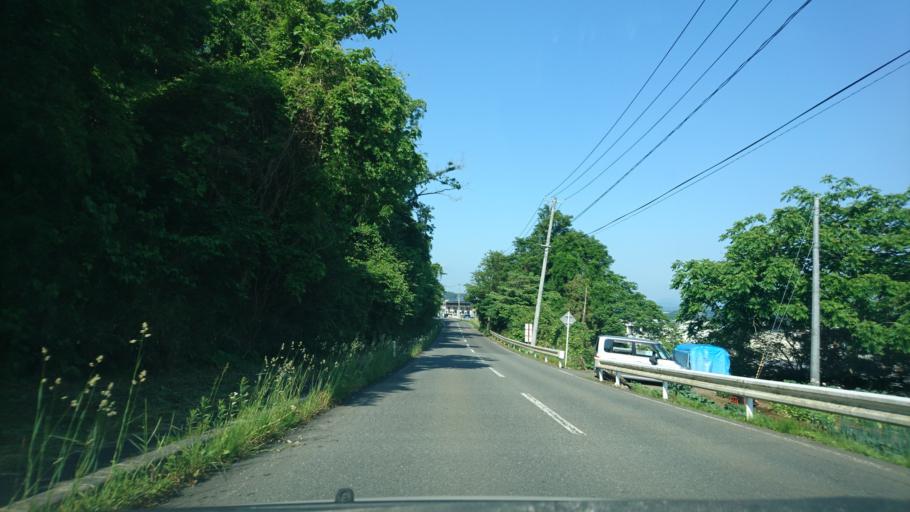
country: JP
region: Iwate
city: Ichinoseki
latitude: 38.9206
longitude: 141.1207
